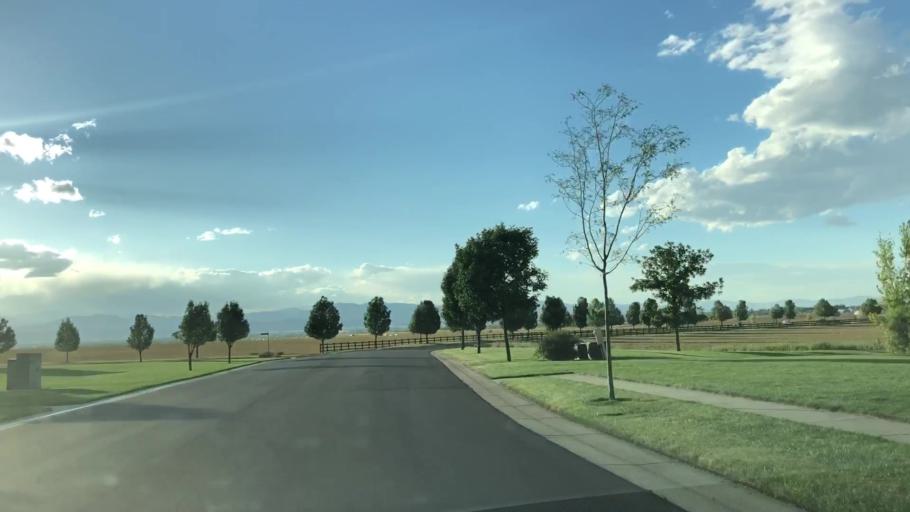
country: US
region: Colorado
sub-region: Larimer County
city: Loveland
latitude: 40.4770
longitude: -105.0066
